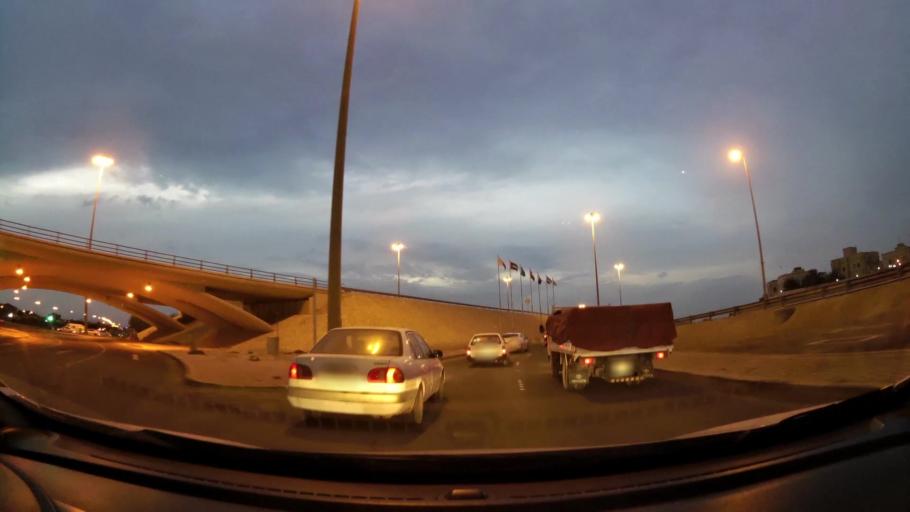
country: BH
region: Central Governorate
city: Madinat Hamad
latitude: 26.1401
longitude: 50.5112
